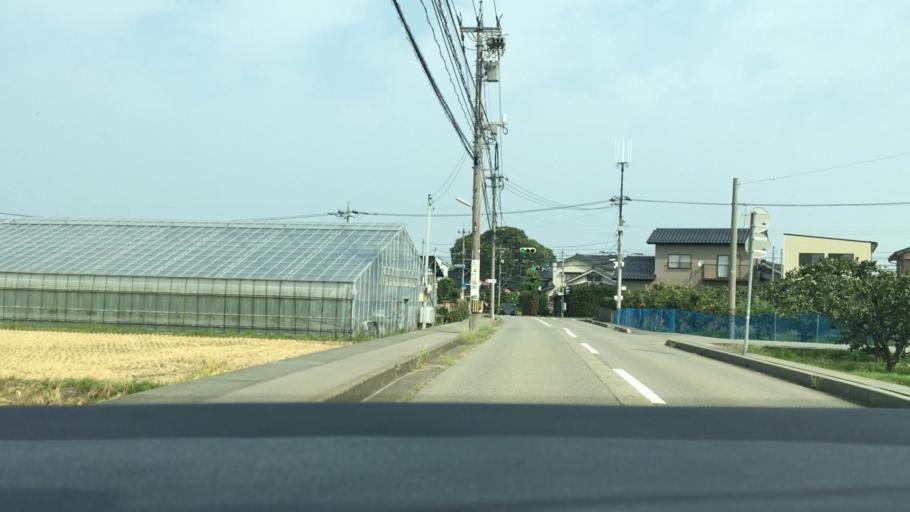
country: JP
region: Ishikawa
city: Nonoichi
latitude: 36.5202
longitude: 136.6043
